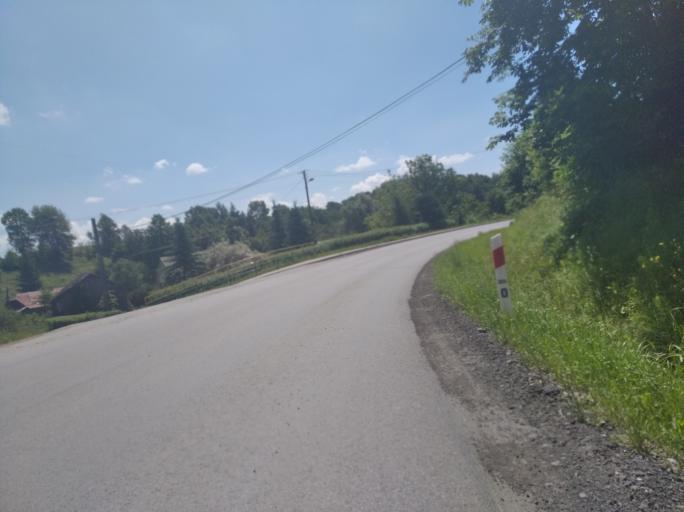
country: PL
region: Subcarpathian Voivodeship
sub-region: Powiat brzozowski
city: Jablonka
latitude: 49.6816
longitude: 22.1187
